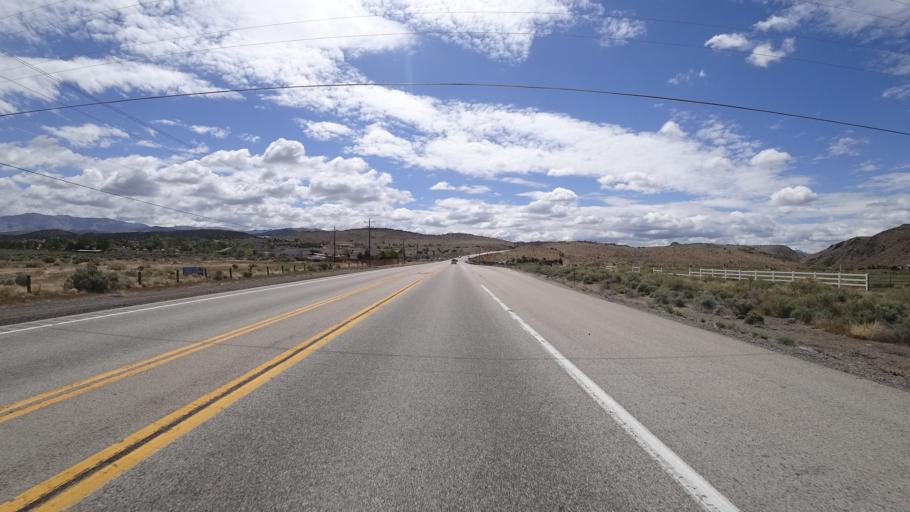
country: US
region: Nevada
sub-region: Douglas County
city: Gardnerville Ranchos
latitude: 38.8818
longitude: -119.6896
